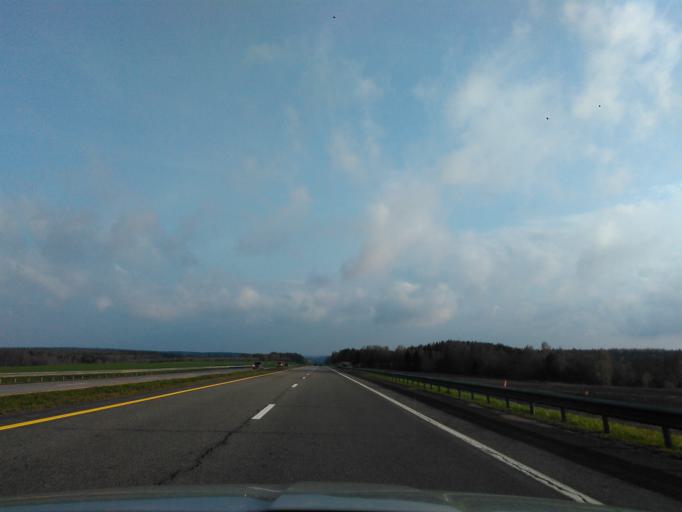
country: BY
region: Minsk
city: Lahoysk
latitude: 54.1491
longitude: 27.8100
